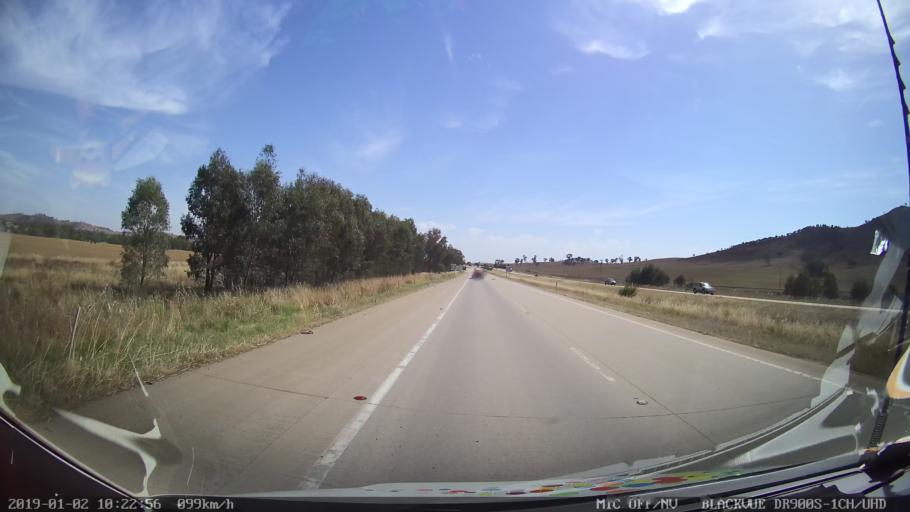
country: AU
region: New South Wales
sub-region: Gundagai
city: Gundagai
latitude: -34.9660
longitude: 148.1532
